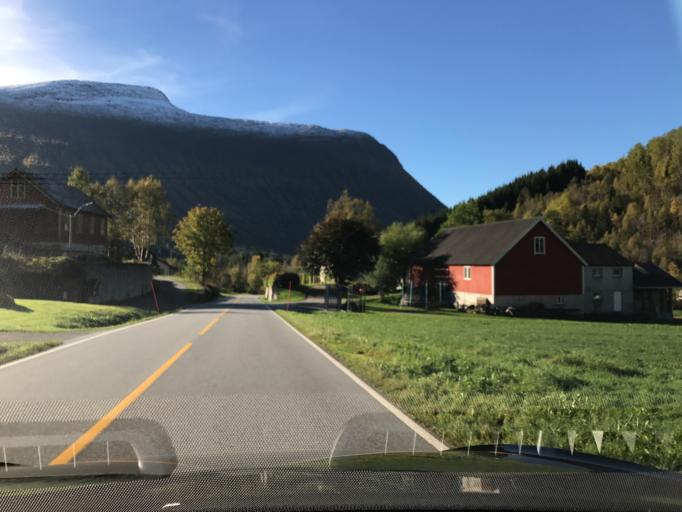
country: NO
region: More og Romsdal
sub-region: Norddal
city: Valldal
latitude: 62.3386
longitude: 7.3919
